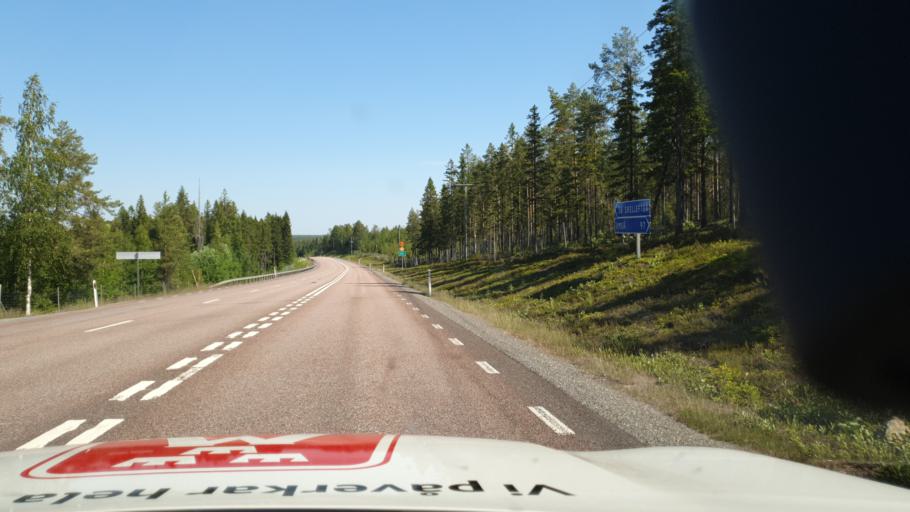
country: SE
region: Vaesterbotten
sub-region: Skelleftea Kommun
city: Burea
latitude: 64.4573
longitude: 21.2884
